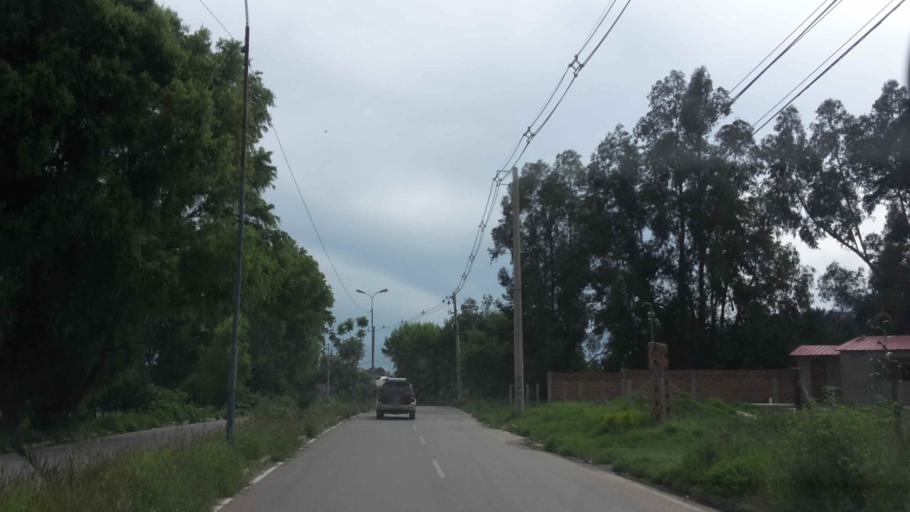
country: BO
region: Cochabamba
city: Cochabamba
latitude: -17.3289
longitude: -66.2471
